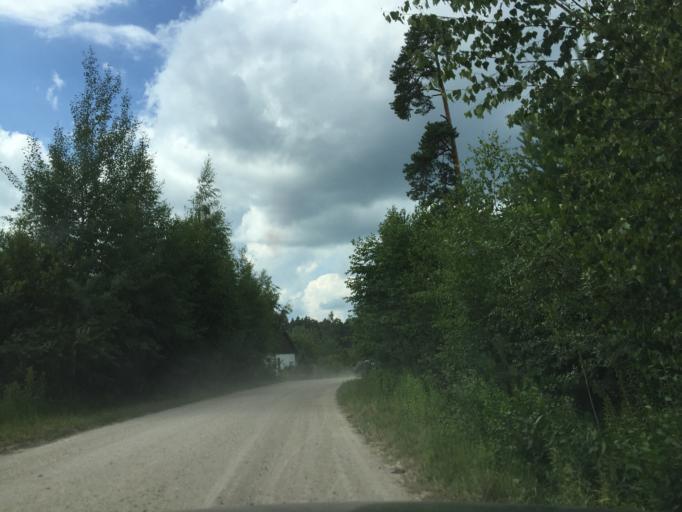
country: LV
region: Jelgava
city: Jelgava
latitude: 56.6268
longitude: 23.6242
